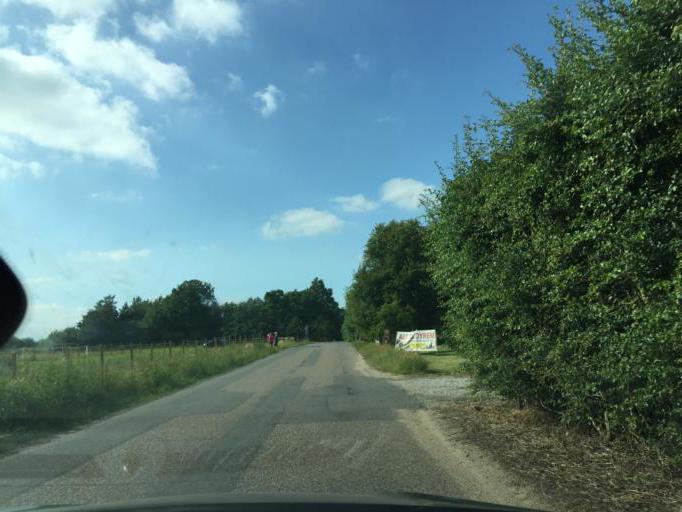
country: DK
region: South Denmark
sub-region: Faaborg-Midtfyn Kommune
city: Arslev
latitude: 55.3227
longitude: 10.5274
